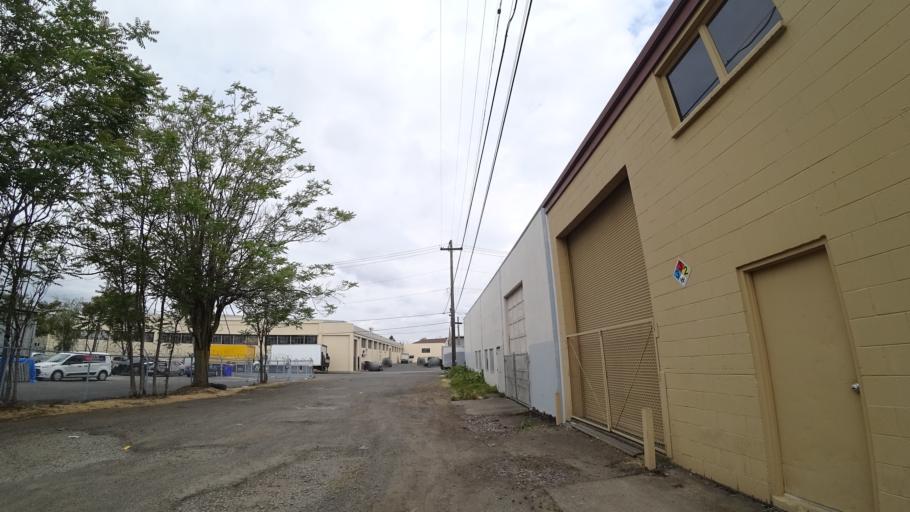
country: US
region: Oregon
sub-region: Clackamas County
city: Milwaukie
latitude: 45.4877
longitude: -122.6406
